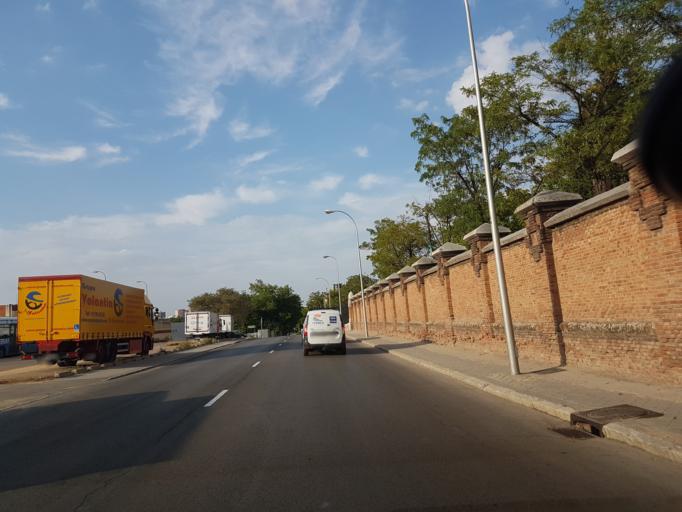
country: ES
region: Madrid
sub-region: Provincia de Madrid
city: Moratalaz
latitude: 40.4233
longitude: -3.6478
